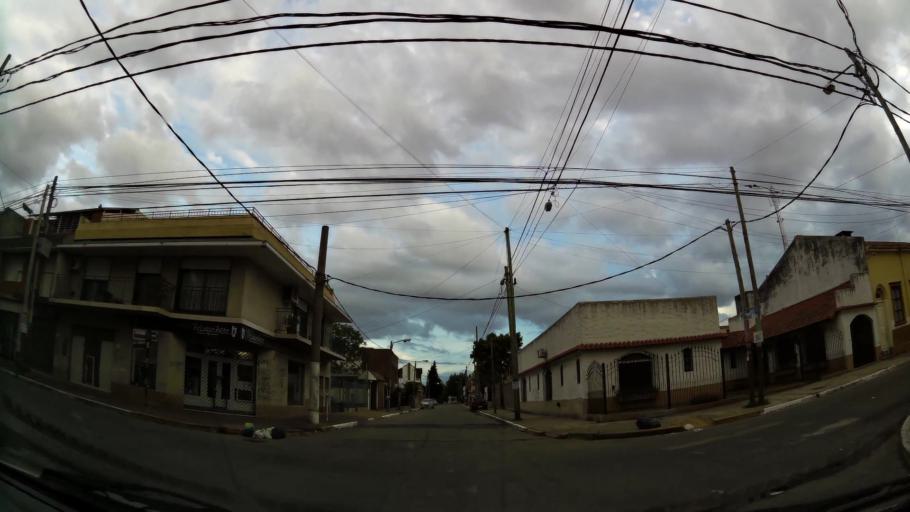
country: AR
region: Buenos Aires
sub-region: Partido de Quilmes
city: Quilmes
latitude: -34.7502
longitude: -58.2333
